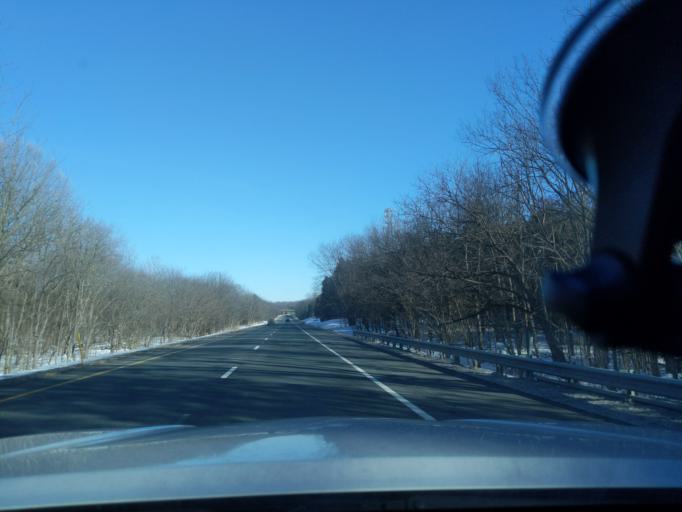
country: US
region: Maryland
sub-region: Washington County
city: Wilson-Conococheague
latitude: 39.6504
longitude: -77.8625
